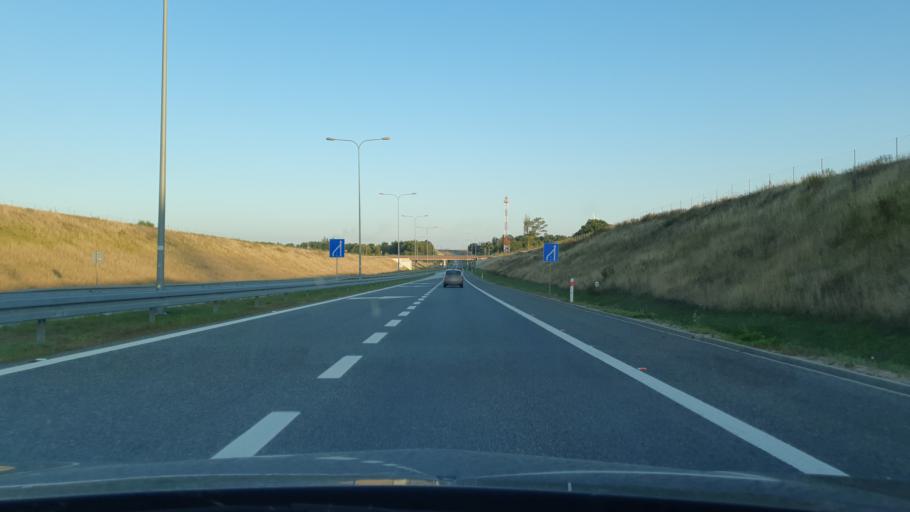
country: PL
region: Pomeranian Voivodeship
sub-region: Powiat slupski
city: Kobylnica
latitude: 54.4346
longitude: 16.9645
